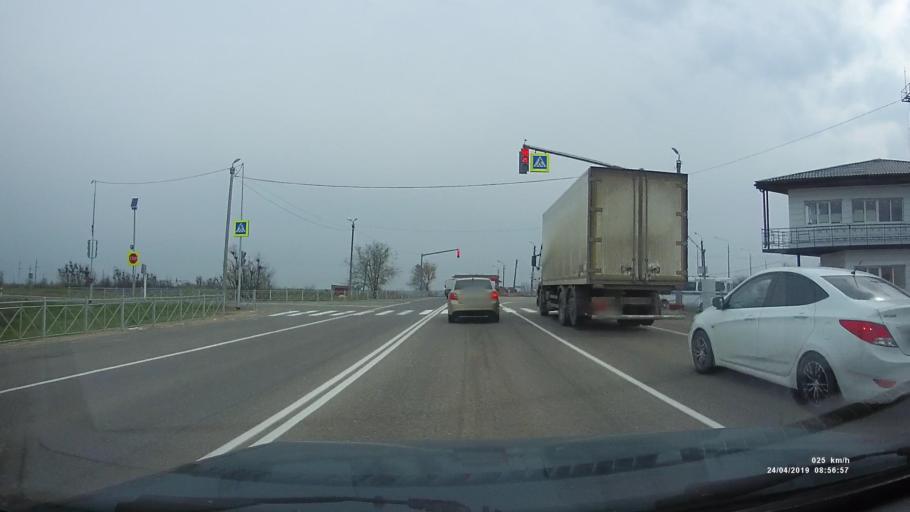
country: RU
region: Kalmykiya
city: Arshan'
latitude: 46.3030
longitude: 44.1881
